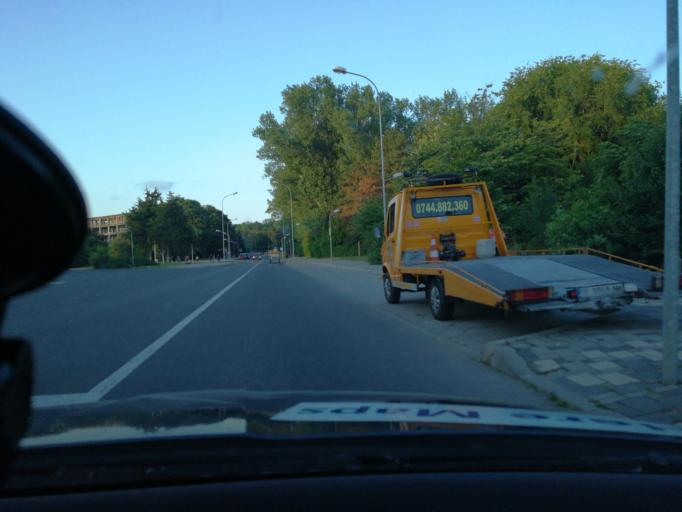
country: RO
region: Constanta
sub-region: Comuna Douazeci si Trei August
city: Douazeci si Trei August
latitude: 43.8720
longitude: 28.5995
